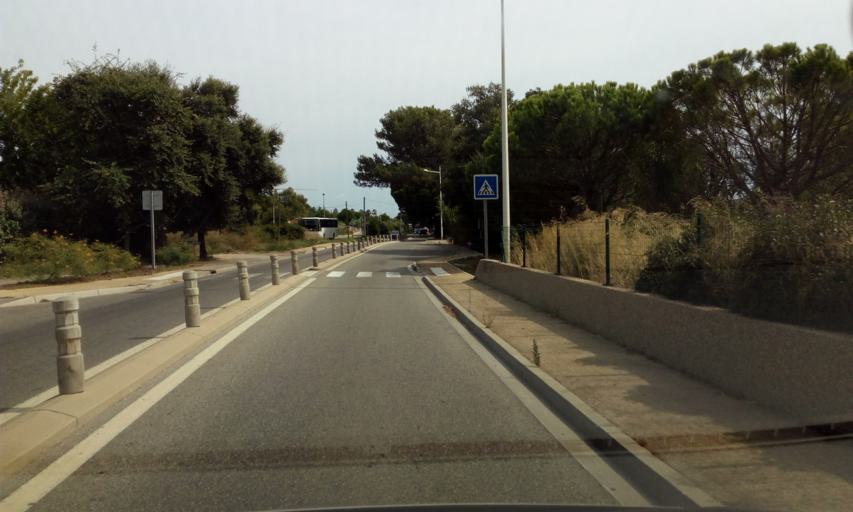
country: FR
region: Provence-Alpes-Cote d'Azur
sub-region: Departement du Var
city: Bormes-les-Mimosas
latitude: 43.1456
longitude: 6.3232
